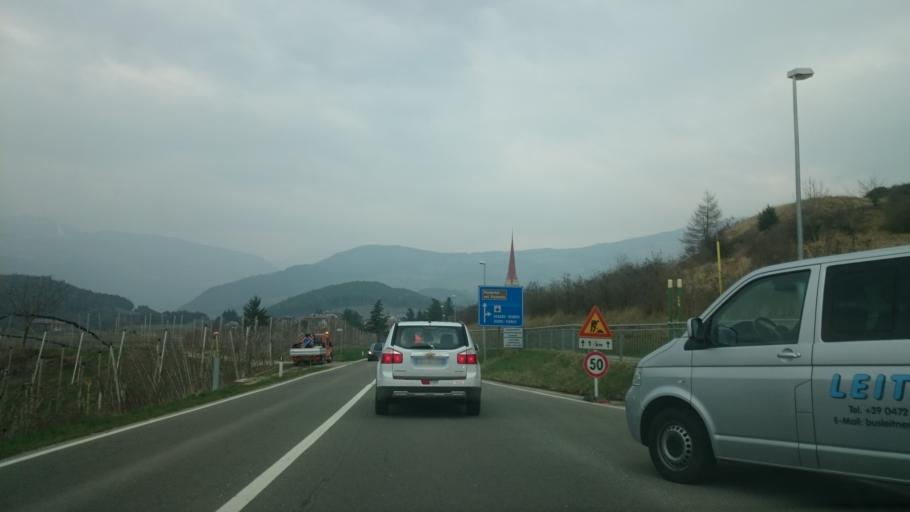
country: IT
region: Trentino-Alto Adige
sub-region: Bolzano
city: Naz-Sciaves - Natz-Schabs
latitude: 46.7670
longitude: 11.6619
